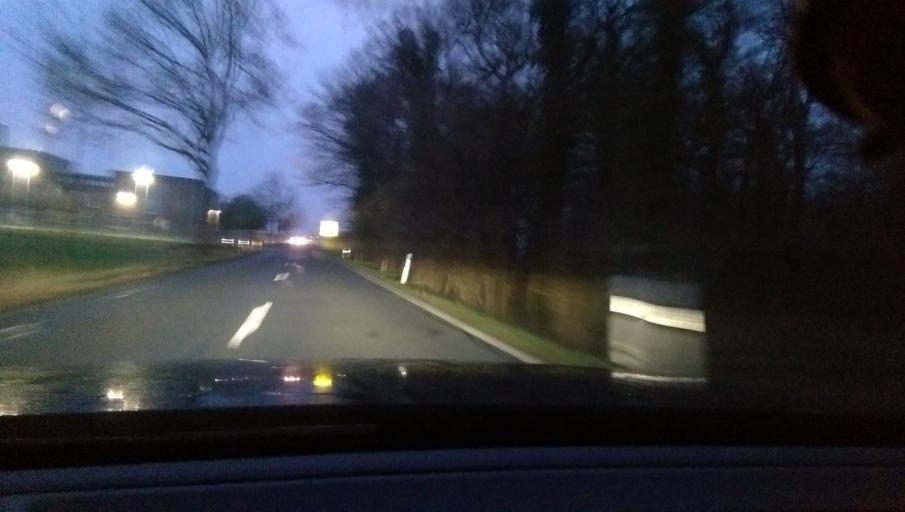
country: DE
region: Lower Saxony
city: Gross Munzel
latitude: 52.3866
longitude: 9.5124
